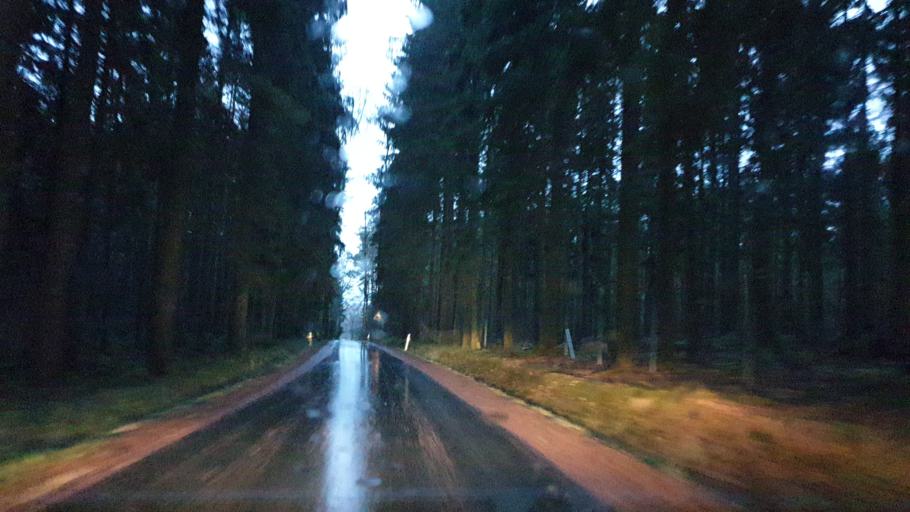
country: DE
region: Saxony
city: Adorf
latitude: 50.3035
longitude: 12.2459
